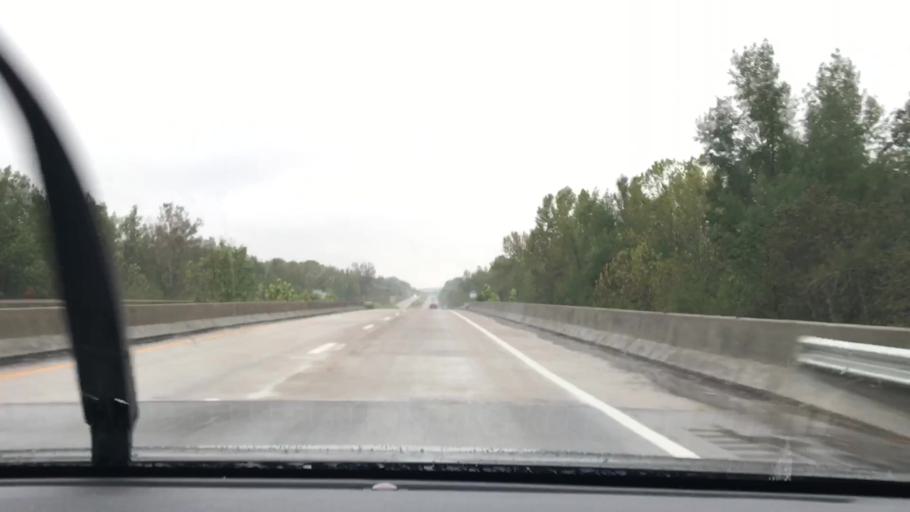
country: US
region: Kentucky
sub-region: Hopkins County
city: Nortonville
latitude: 37.1895
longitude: -87.4430
